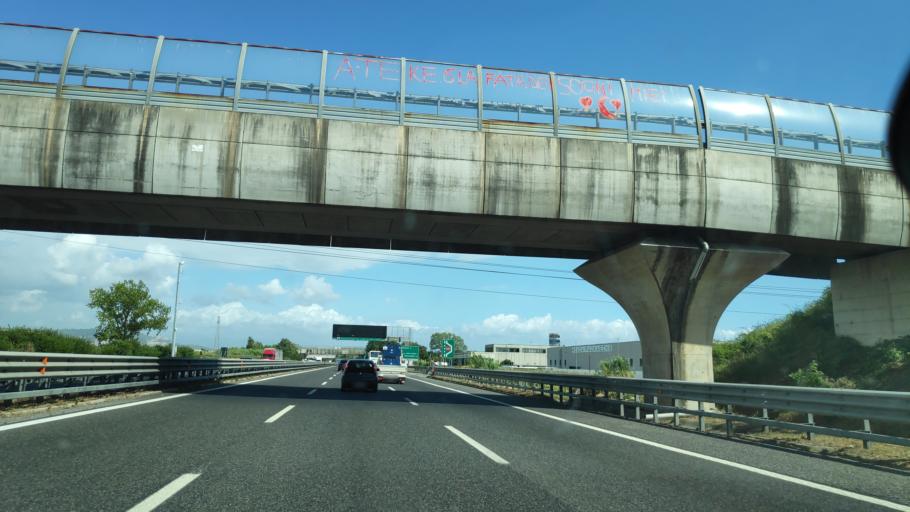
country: IT
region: Campania
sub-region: Provincia di Salerno
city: Sant'Antonio
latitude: 40.6391
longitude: 14.9019
